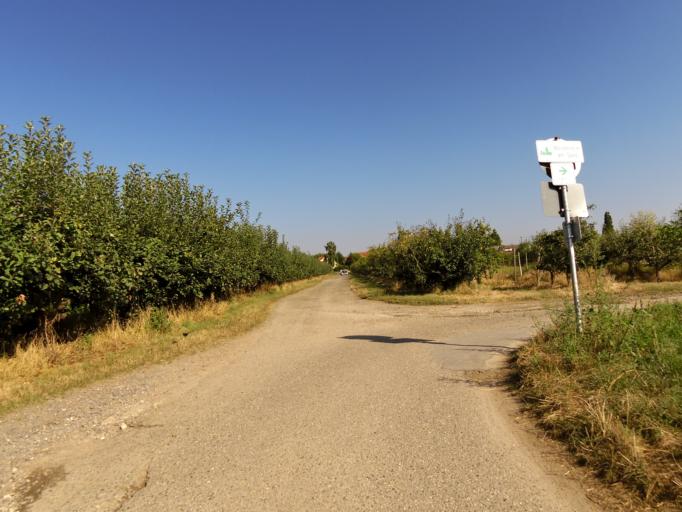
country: DE
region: Rheinland-Pfalz
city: Weisenheim am Sand
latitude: 49.5135
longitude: 8.2405
